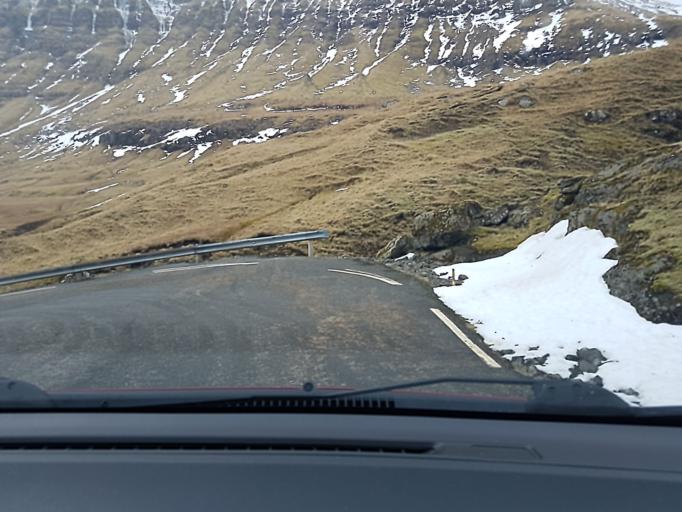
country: FO
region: Streymoy
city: Kollafjordhur
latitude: 62.0494
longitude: -6.9221
